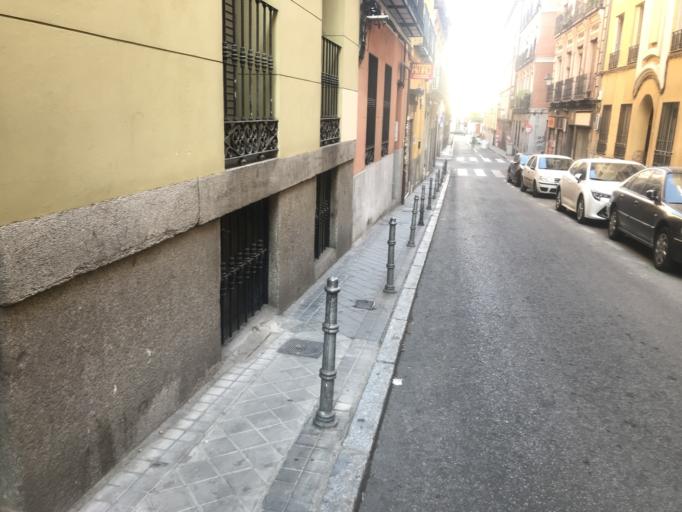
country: ES
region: Madrid
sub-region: Provincia de Madrid
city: Chamberi
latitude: 40.4284
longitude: -3.7079
